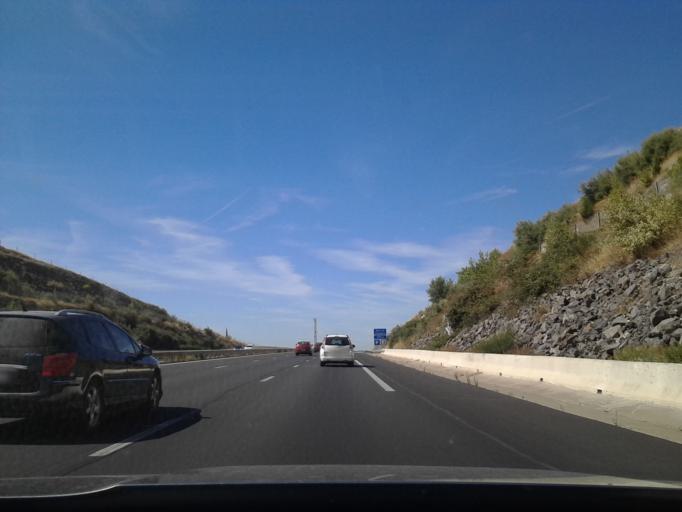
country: FR
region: Languedoc-Roussillon
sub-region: Departement de l'Herault
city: Lespignan
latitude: 43.2706
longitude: 3.1798
